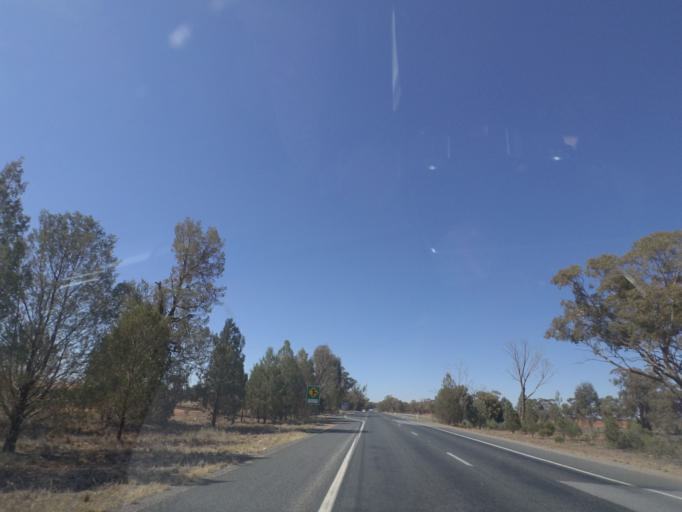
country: AU
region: New South Wales
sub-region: Bland
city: West Wyalong
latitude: -34.1976
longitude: 147.1107
